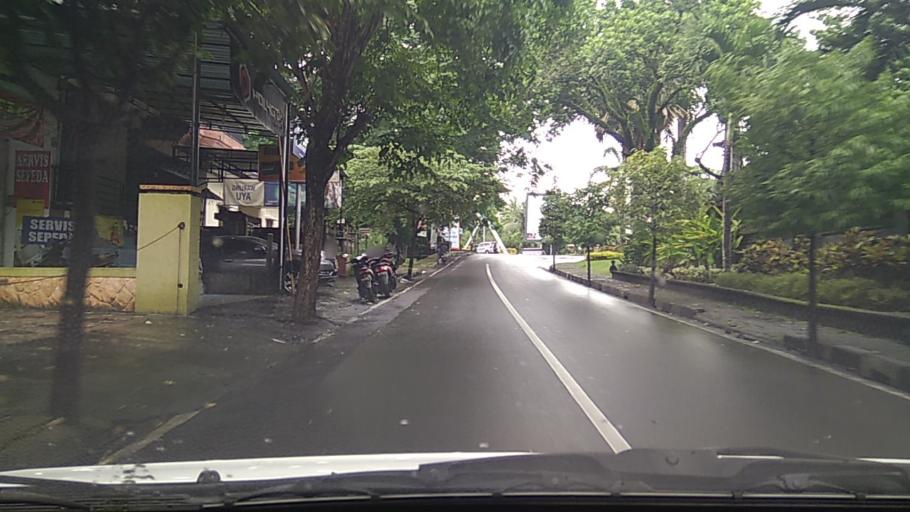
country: ID
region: Bali
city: Subagan
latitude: -8.4479
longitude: 115.6095
